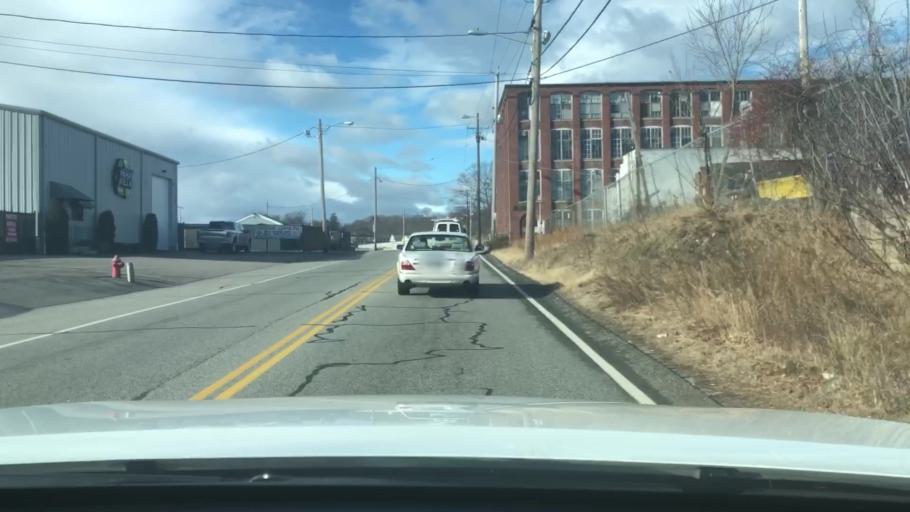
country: US
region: Rhode Island
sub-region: Providence County
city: Woonsocket
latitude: 42.0147
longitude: -71.5097
